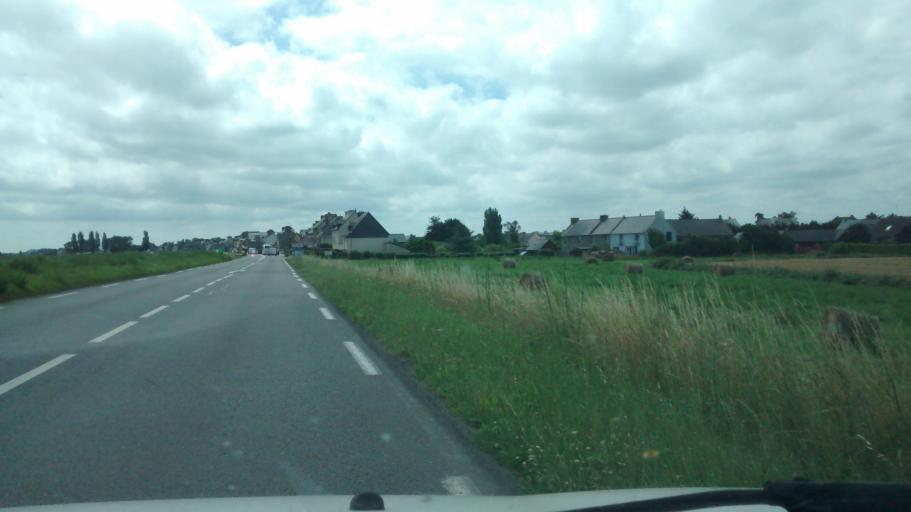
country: FR
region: Brittany
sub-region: Departement d'Ille-et-Vilaine
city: La Fresnais
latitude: 48.6256
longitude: -1.8586
